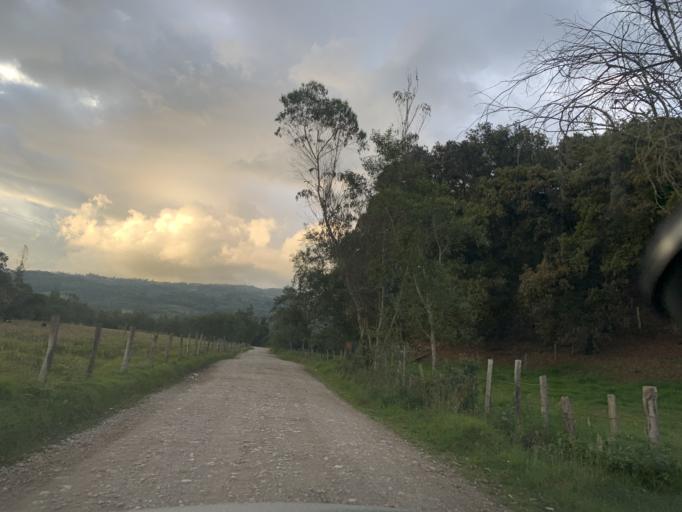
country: CO
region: Boyaca
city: La Capilla
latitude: 5.7310
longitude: -73.4947
